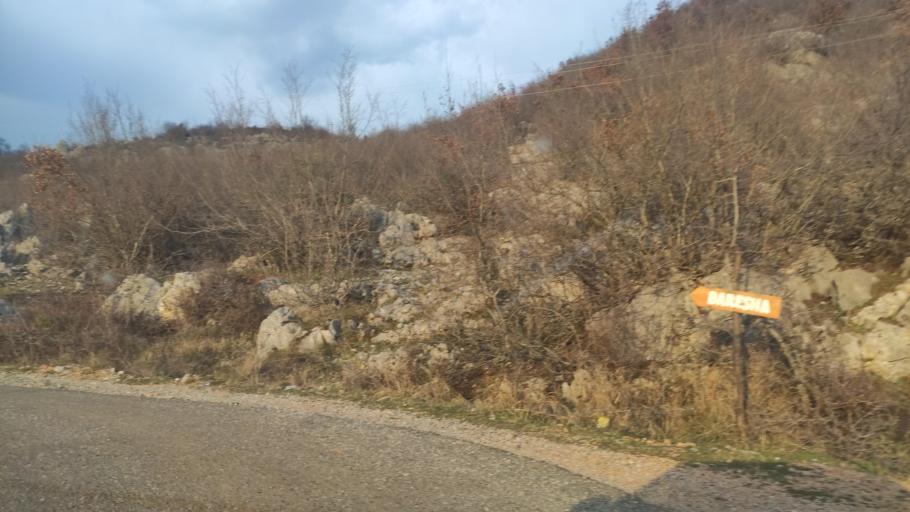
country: AL
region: Shkoder
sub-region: Rrethi i Malesia e Madhe
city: Gruemire
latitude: 42.2385
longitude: 19.5371
